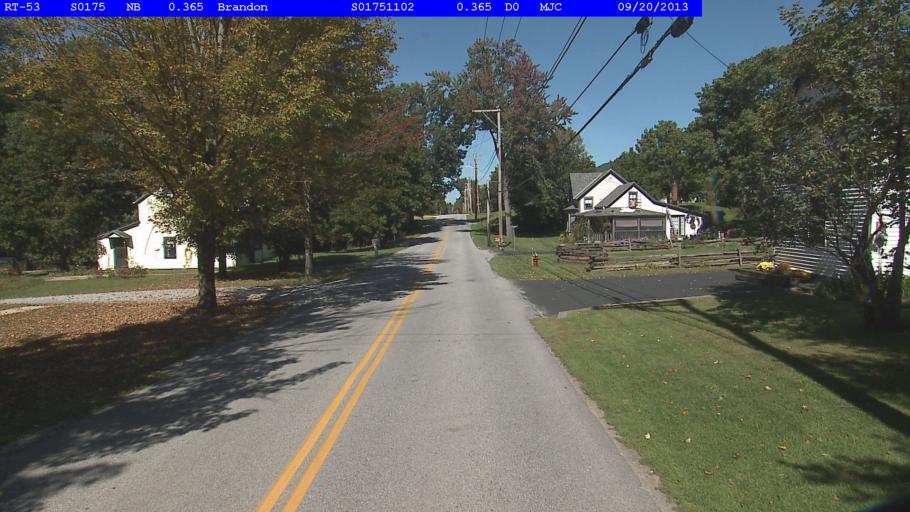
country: US
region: Vermont
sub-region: Rutland County
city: Brandon
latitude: 43.8320
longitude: -73.0552
